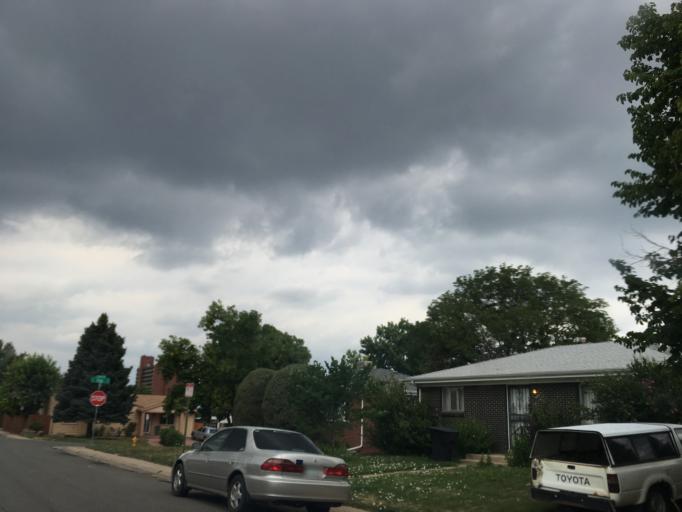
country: US
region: Colorado
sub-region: Arapahoe County
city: Sheridan
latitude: 39.6841
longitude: -105.0199
